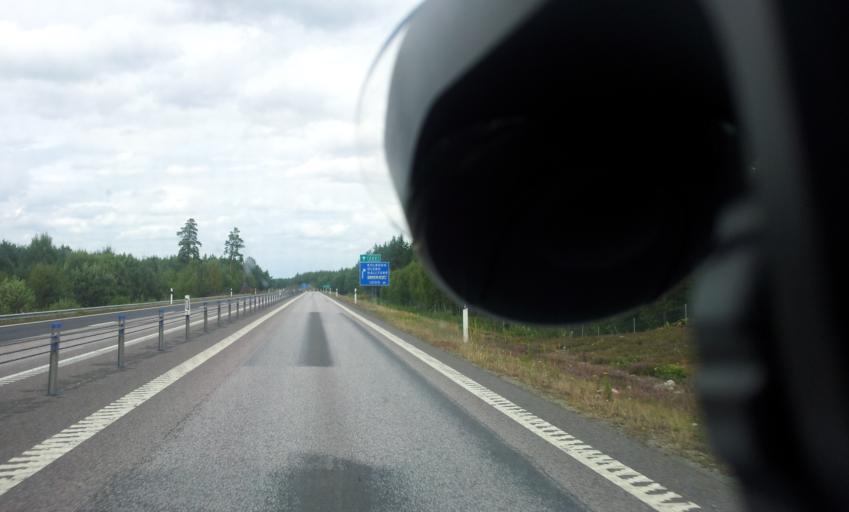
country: SE
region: Kalmar
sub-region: Torsas Kommun
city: Torsas
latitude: 56.4875
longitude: 16.0838
